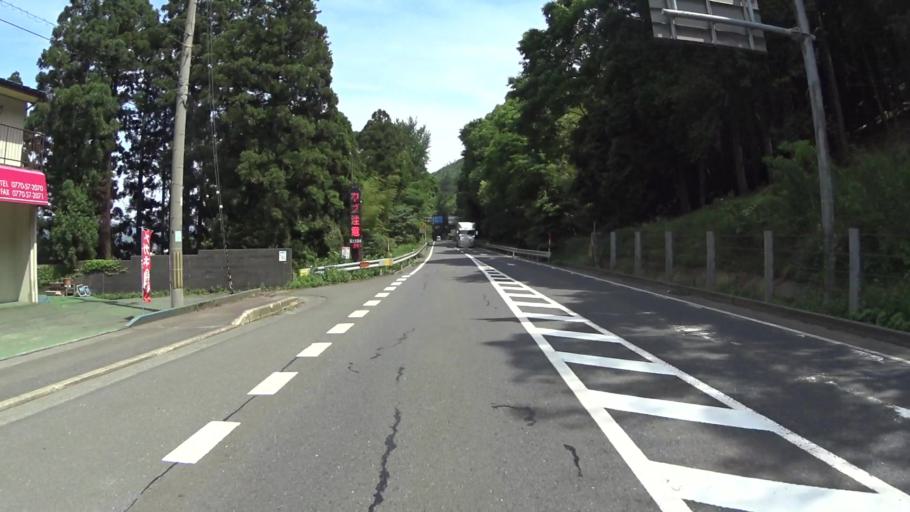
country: JP
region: Fukui
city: Obama
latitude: 35.4717
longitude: 135.8061
